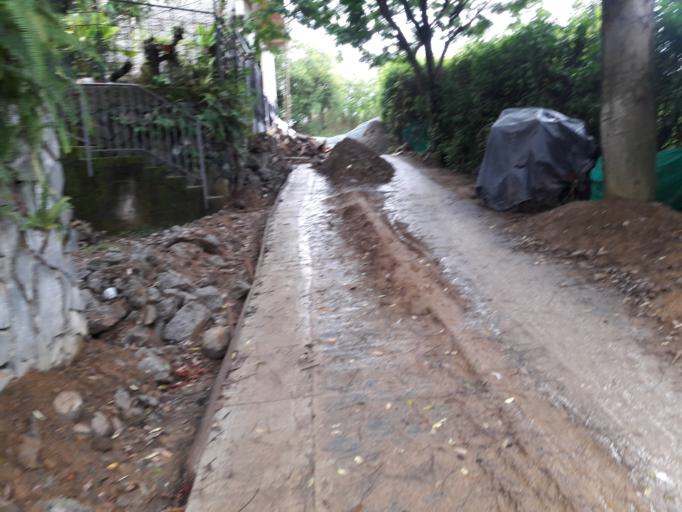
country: CO
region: Valle del Cauca
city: Cali
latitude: 3.4730
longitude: -76.5553
